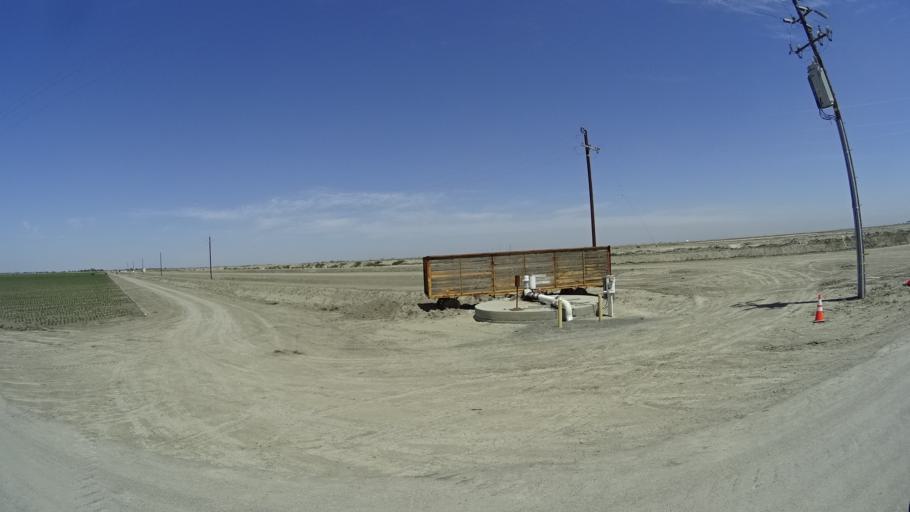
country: US
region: California
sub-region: Kings County
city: Stratford
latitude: 36.1233
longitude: -119.6997
